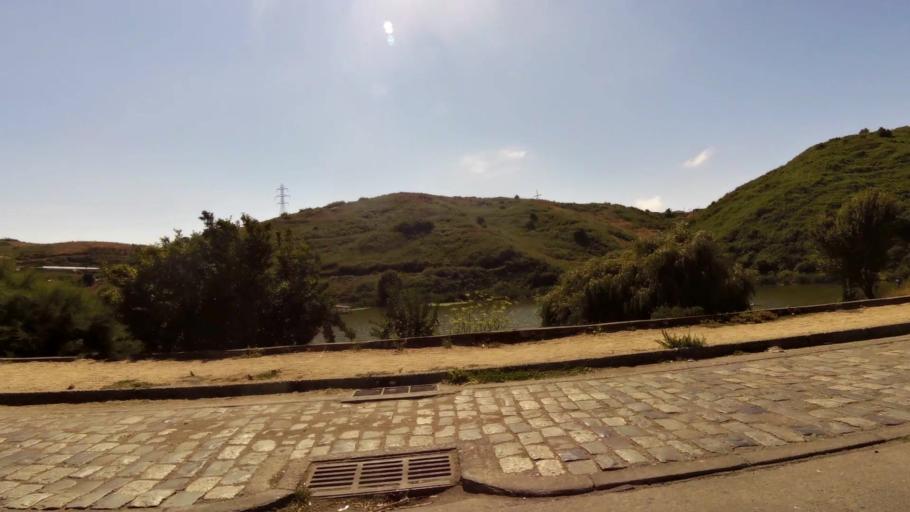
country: CL
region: Biobio
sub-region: Provincia de Concepcion
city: Concepcion
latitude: -36.7999
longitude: -73.0405
